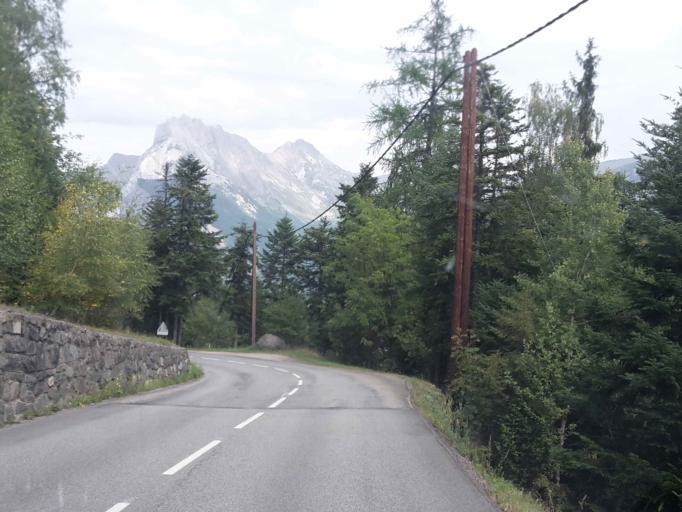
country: FR
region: Rhone-Alpes
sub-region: Departement de la Savoie
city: Saint-Michel-de-Maurienne
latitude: 45.2005
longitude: 6.4676
